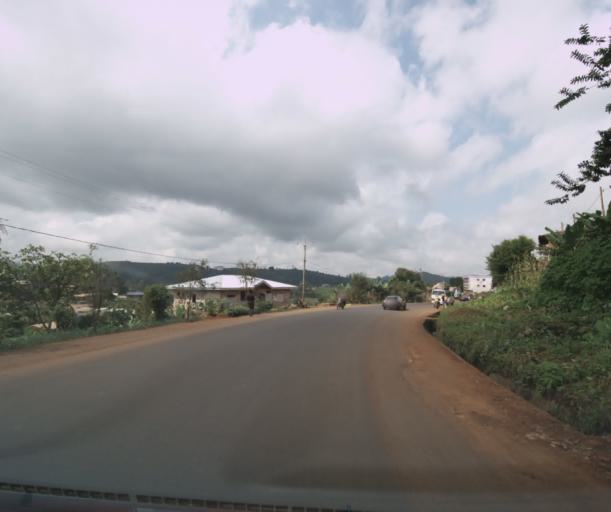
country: CM
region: West
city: Dschang
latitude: 5.4551
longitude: 10.0688
